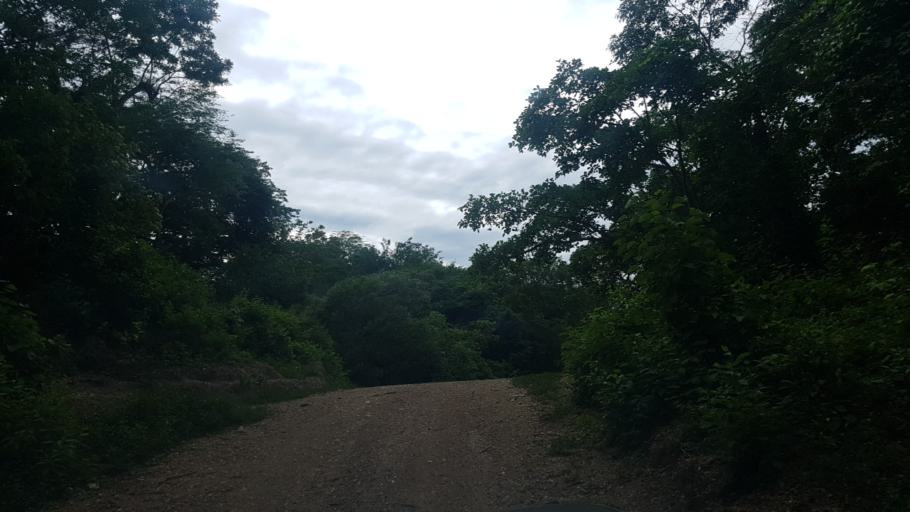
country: NI
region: Nueva Segovia
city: Ocotal
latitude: 13.5990
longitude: -86.4223
